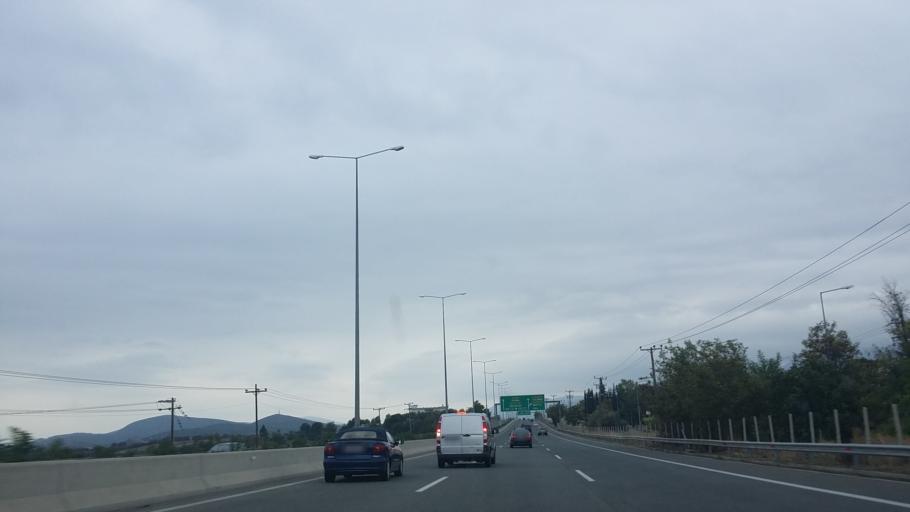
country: GR
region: Central Greece
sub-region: Nomos Voiotias
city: Oinofyta
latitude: 38.2982
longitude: 23.6628
